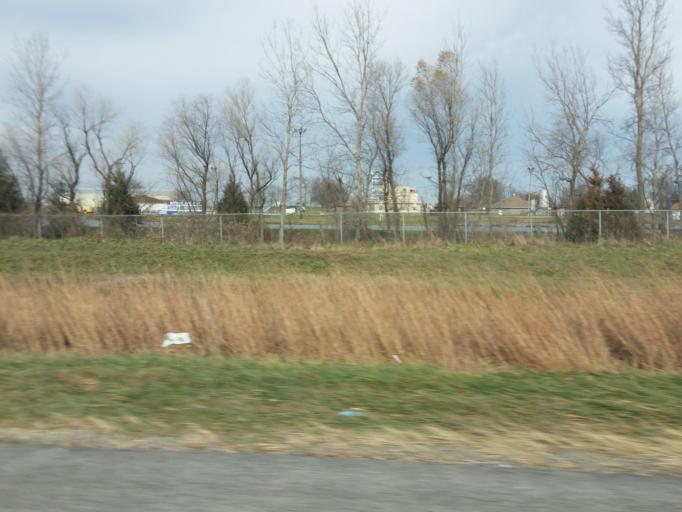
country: US
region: Iowa
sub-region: Scott County
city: Eldridge
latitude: 41.6007
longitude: -90.6355
